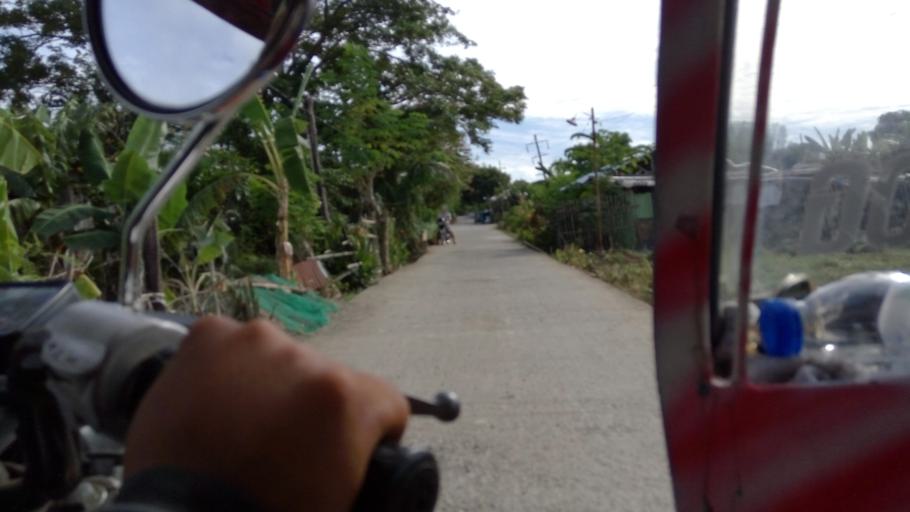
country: PH
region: Ilocos
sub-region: Province of La Union
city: San Eugenio
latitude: 16.3560
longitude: 120.3526
